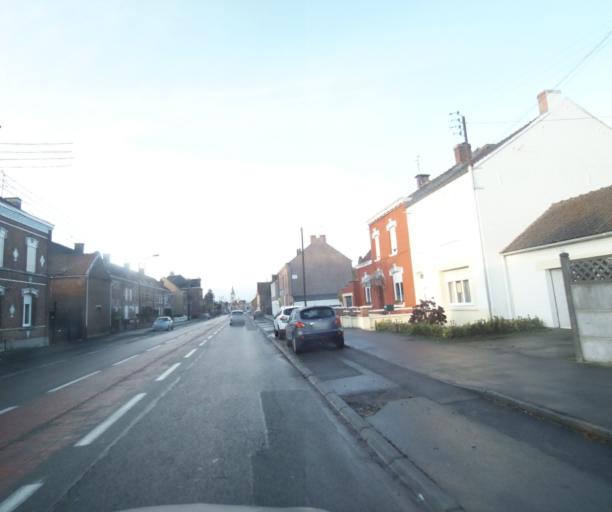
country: FR
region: Nord-Pas-de-Calais
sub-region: Departement du Nord
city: Onnaing
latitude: 50.3886
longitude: 3.6076
